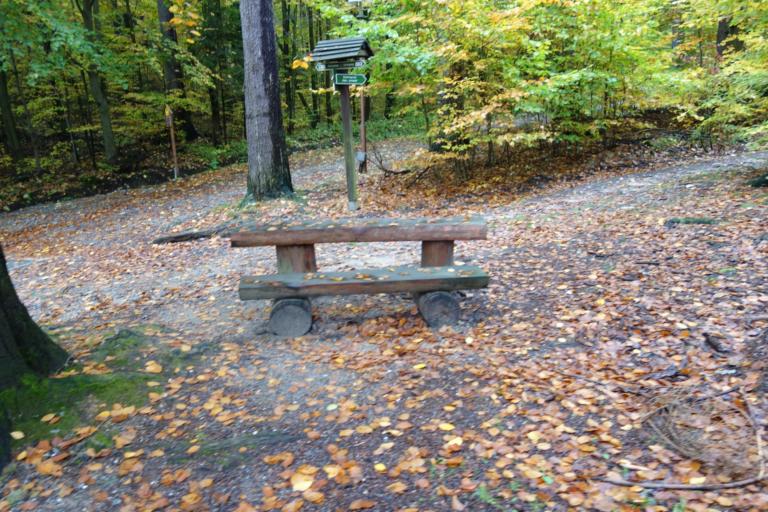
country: DE
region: Saxony
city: Kurort Oybin
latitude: 50.8374
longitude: 14.7307
